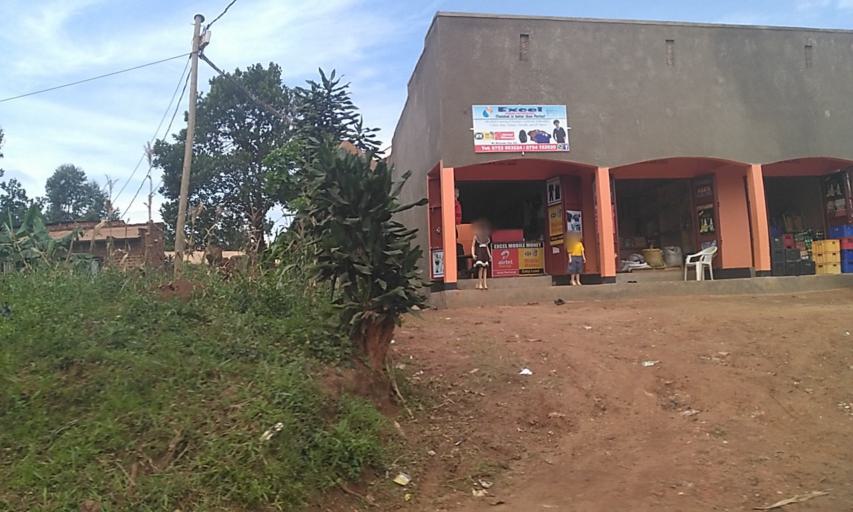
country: UG
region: Central Region
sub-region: Wakiso District
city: Kajansi
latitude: 0.2804
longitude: 32.5172
